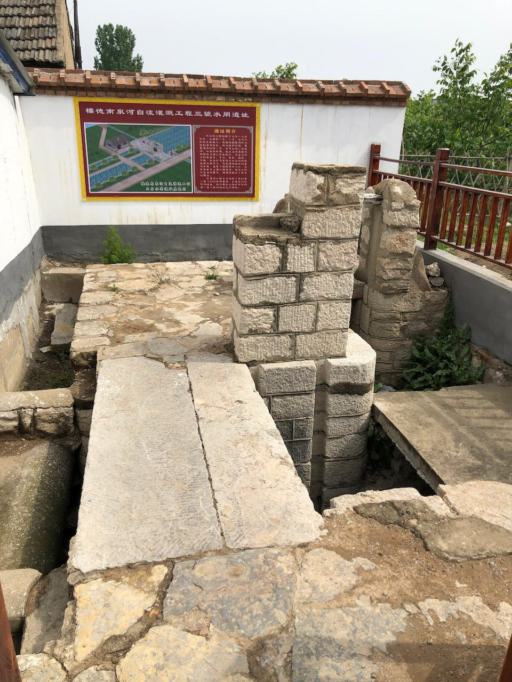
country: CN
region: Shandong Sheng
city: Sishui
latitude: 35.8681
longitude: 117.2971
